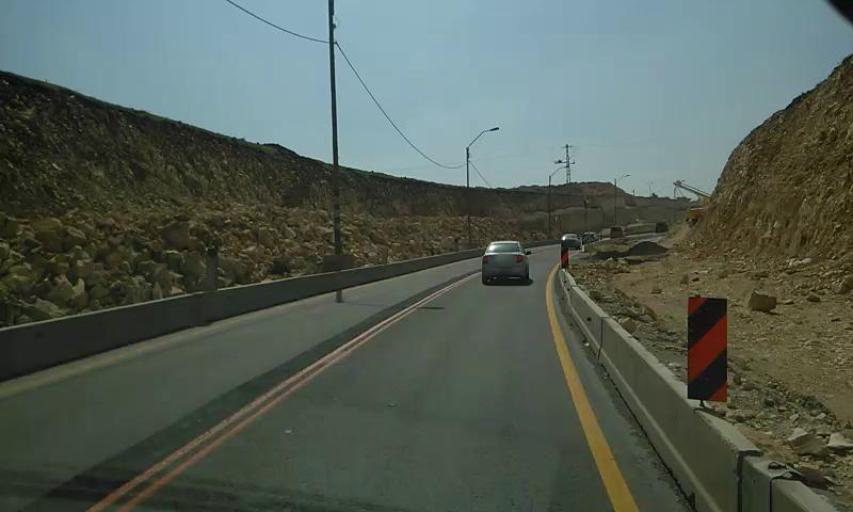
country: PS
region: West Bank
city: Jaba`
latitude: 31.8557
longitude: 35.2656
